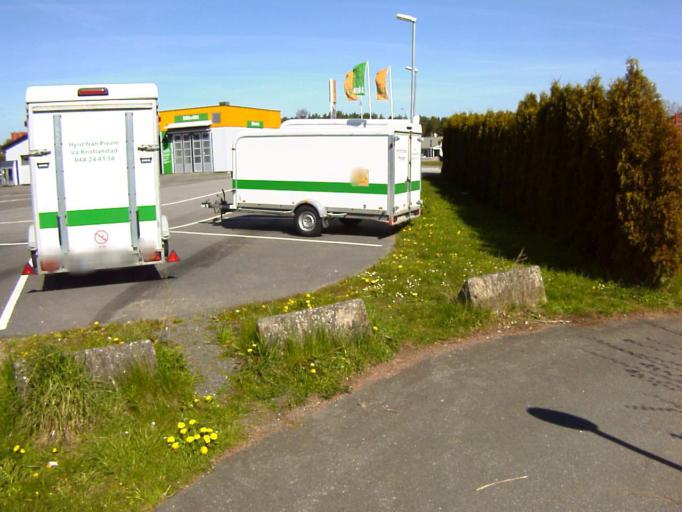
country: SE
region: Skane
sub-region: Kristianstads Kommun
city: Norra Asum
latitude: 56.0013
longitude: 14.0942
